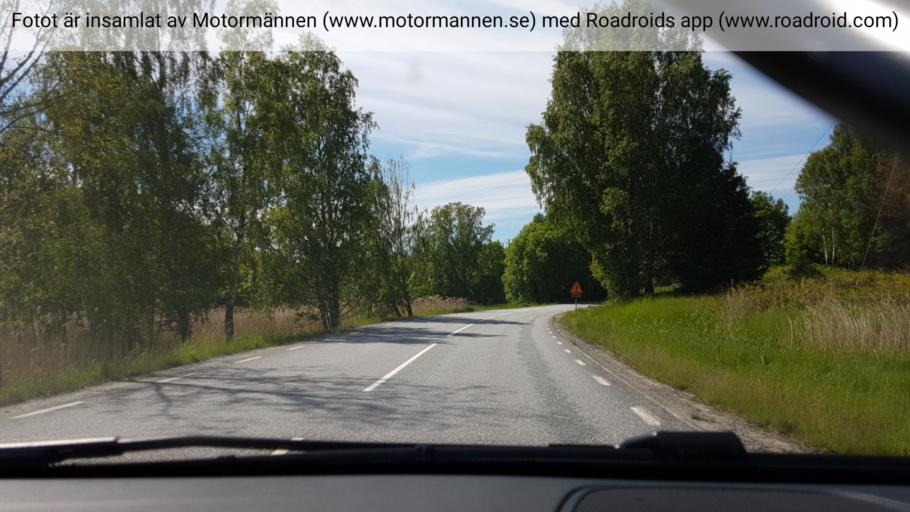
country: SE
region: Stockholm
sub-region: Nynashamns Kommun
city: Nynashamn
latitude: 58.9564
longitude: 17.9711
